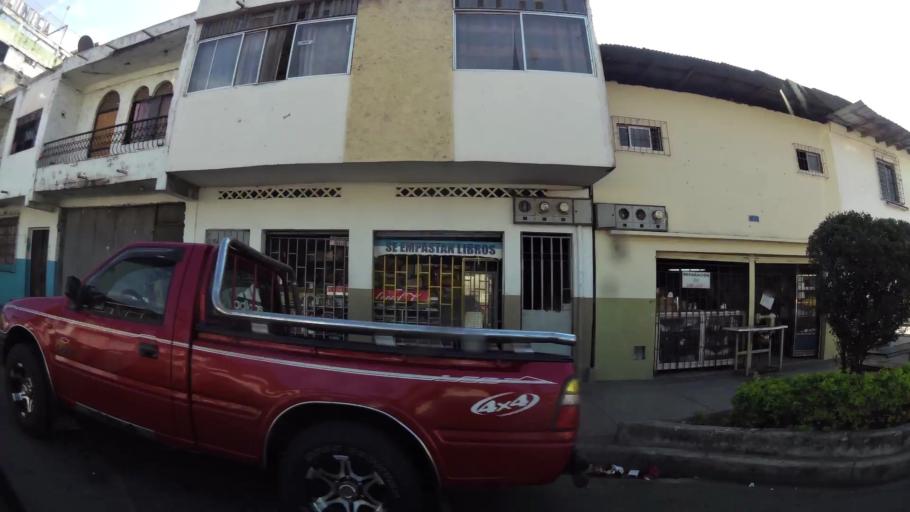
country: EC
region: Guayas
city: Guayaquil
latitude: -2.1979
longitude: -79.9149
